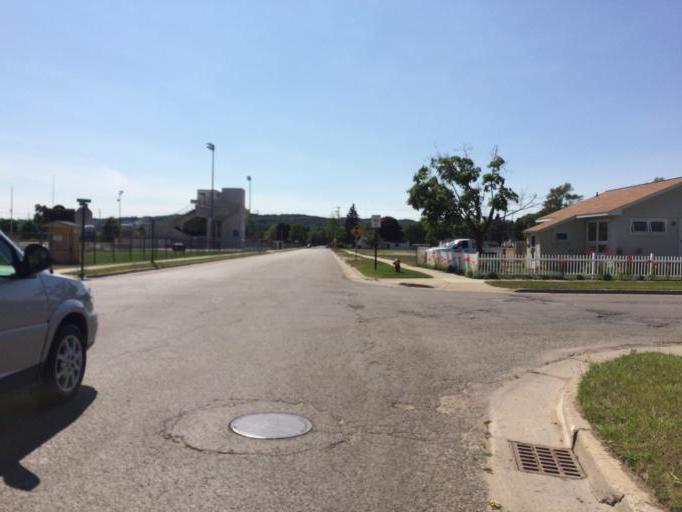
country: US
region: Michigan
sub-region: Grand Traverse County
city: Traverse City
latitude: 44.7535
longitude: -85.6258
